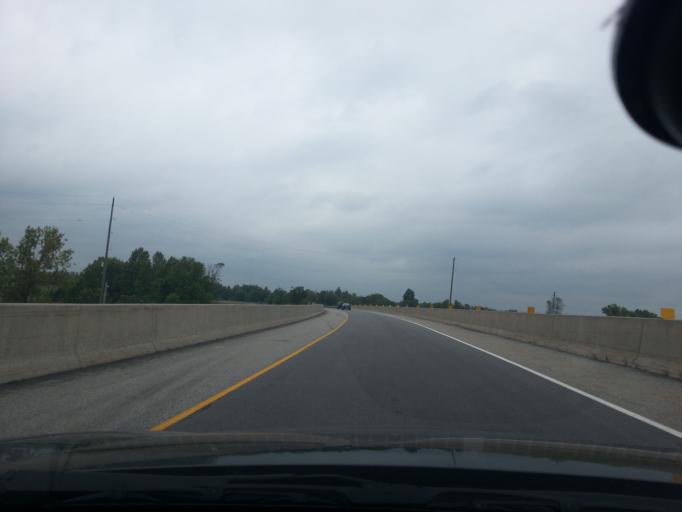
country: CA
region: Ontario
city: Prescott
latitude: 44.7475
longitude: -75.4884
